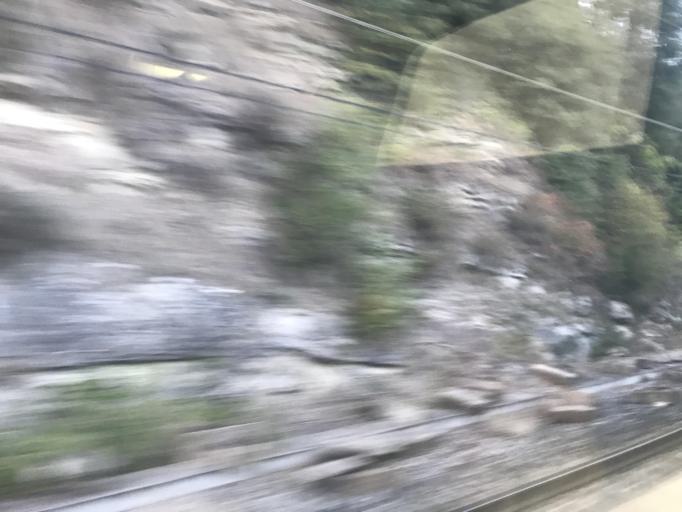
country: ES
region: Basque Country
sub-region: Provincia de Alava
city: Arminon
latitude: 42.7316
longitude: -2.8750
